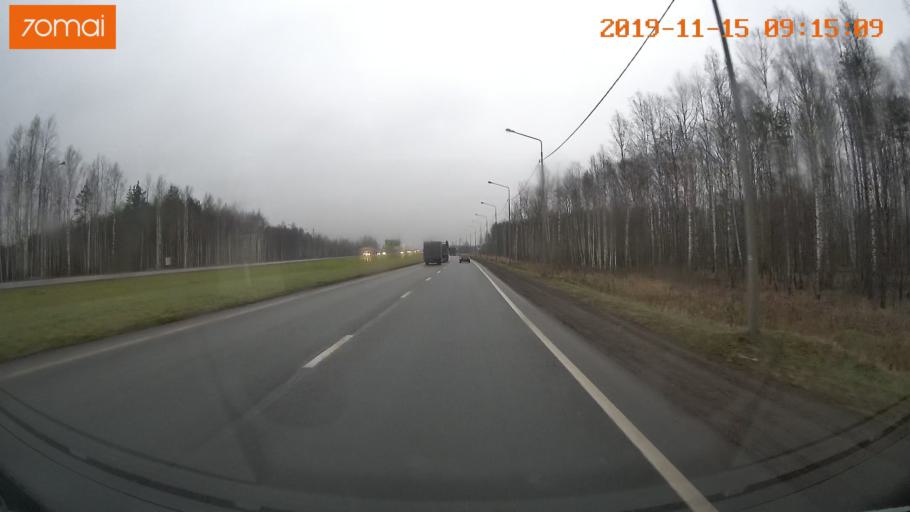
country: RU
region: Vologda
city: Tonshalovo
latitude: 59.2354
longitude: 37.9648
